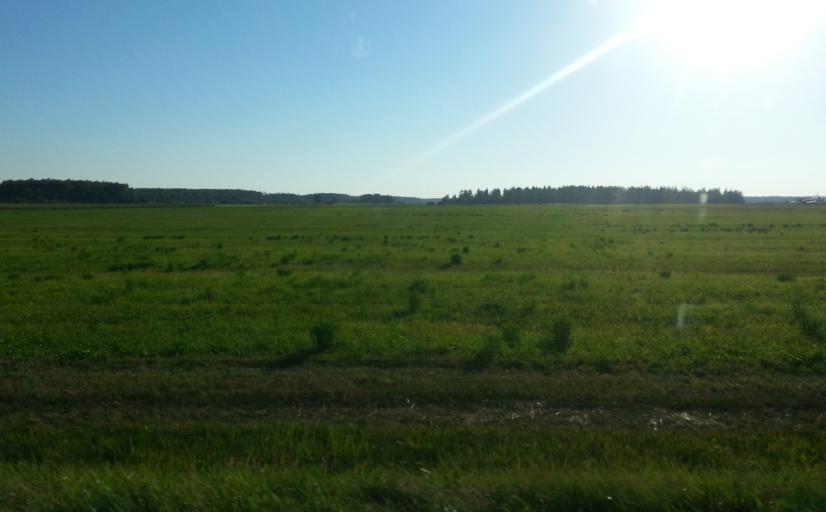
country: LT
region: Panevezys
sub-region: Panevezys City
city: Panevezys
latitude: 55.8263
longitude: 24.3667
